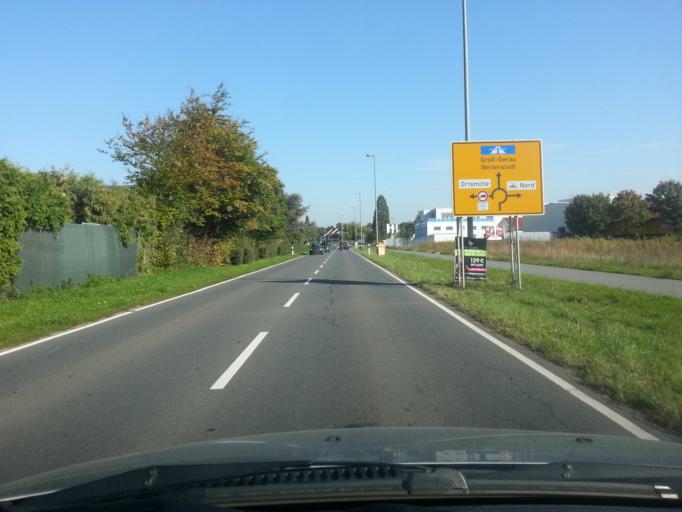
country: DE
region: Hesse
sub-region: Regierungsbezirk Darmstadt
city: Buttelborn
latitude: 49.8971
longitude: 8.5196
